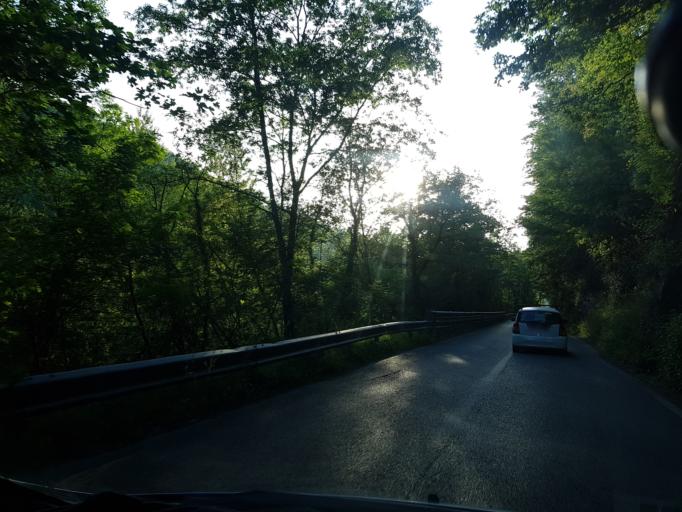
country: IT
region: Tuscany
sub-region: Provincia di Massa-Carrara
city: Casola in Lunigiana
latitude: 44.1921
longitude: 10.1319
